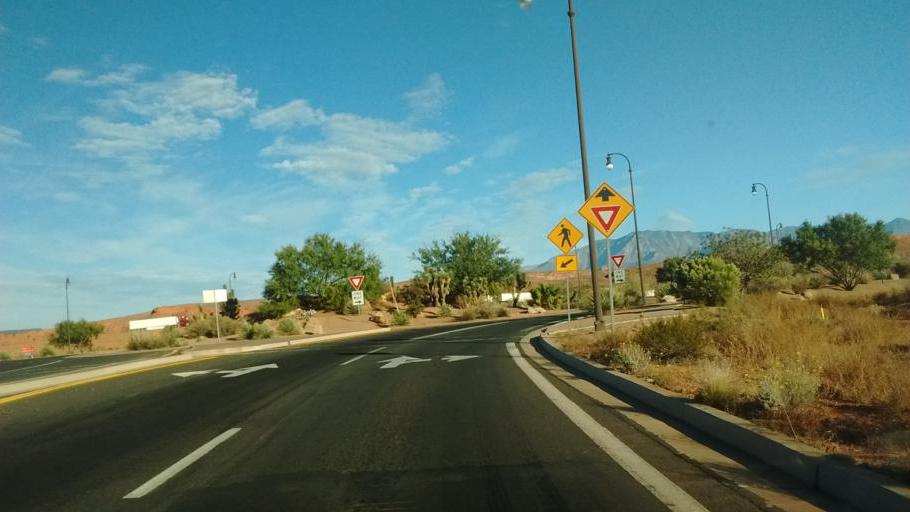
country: US
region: Utah
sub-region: Washington County
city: Washington
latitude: 37.1440
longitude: -113.4856
